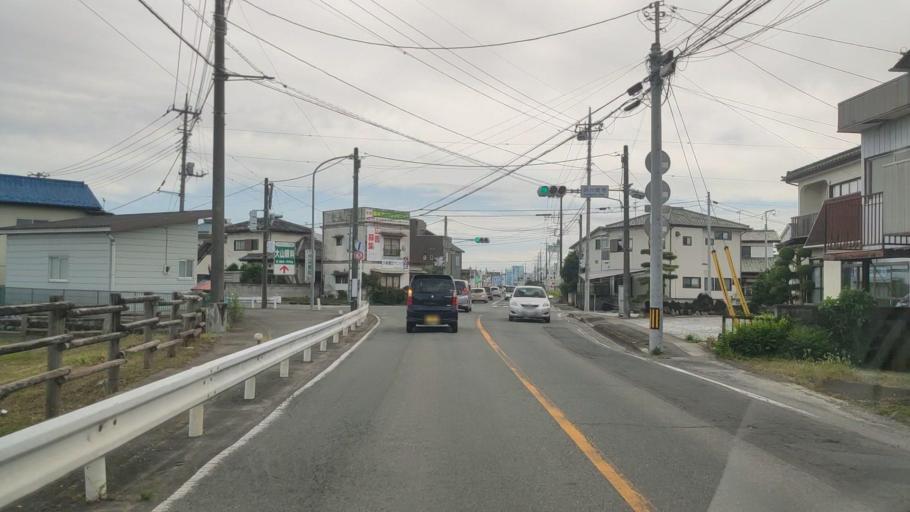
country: JP
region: Gunma
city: Takasaki
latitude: 36.3631
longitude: 138.9778
